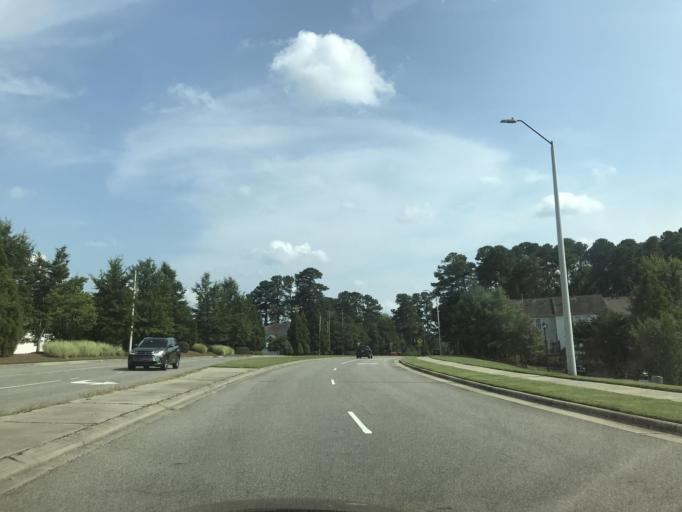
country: US
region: North Carolina
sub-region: Wake County
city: Morrisville
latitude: 35.8358
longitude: -78.8623
